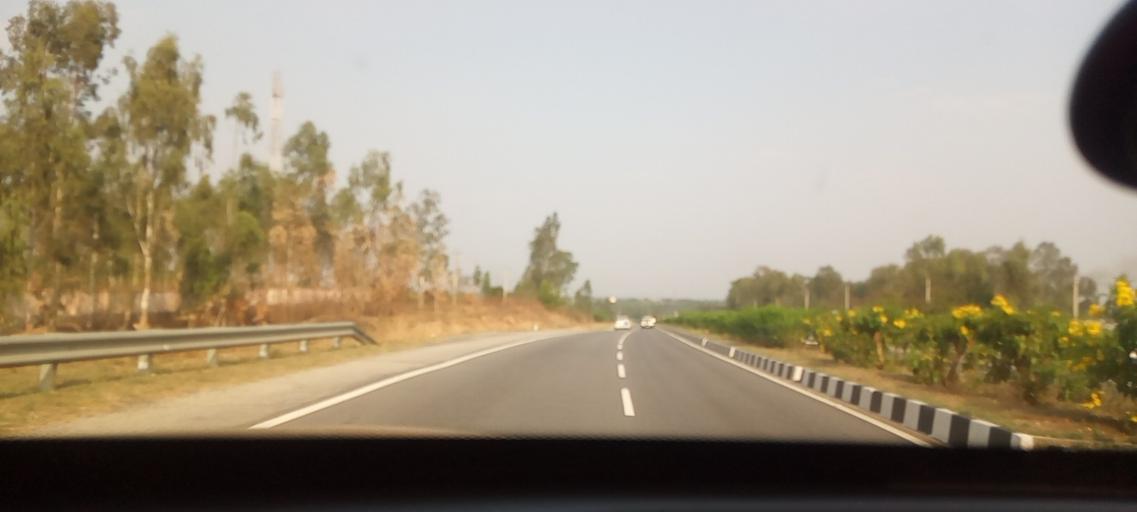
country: IN
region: Karnataka
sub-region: Hassan
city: Channarayapatna
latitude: 12.9744
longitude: 76.2733
